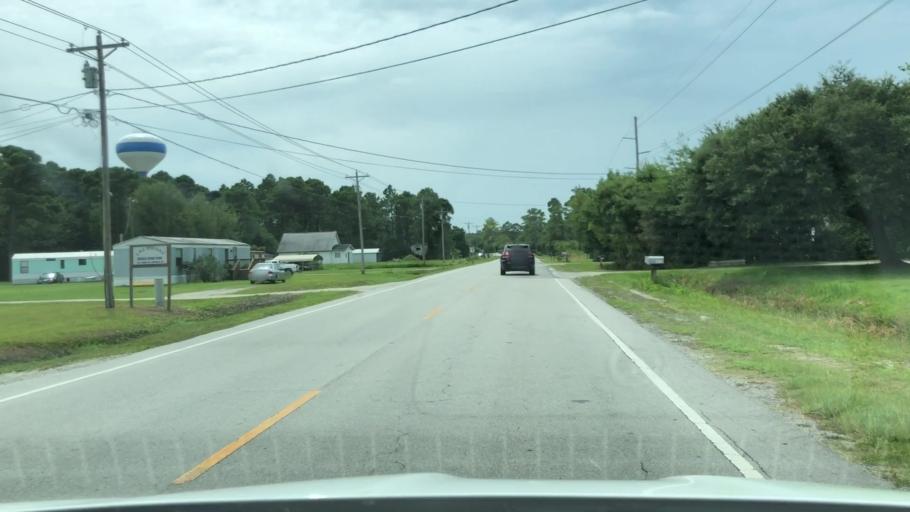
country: US
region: North Carolina
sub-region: Carteret County
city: Broad Creek
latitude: 34.7355
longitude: -76.8878
